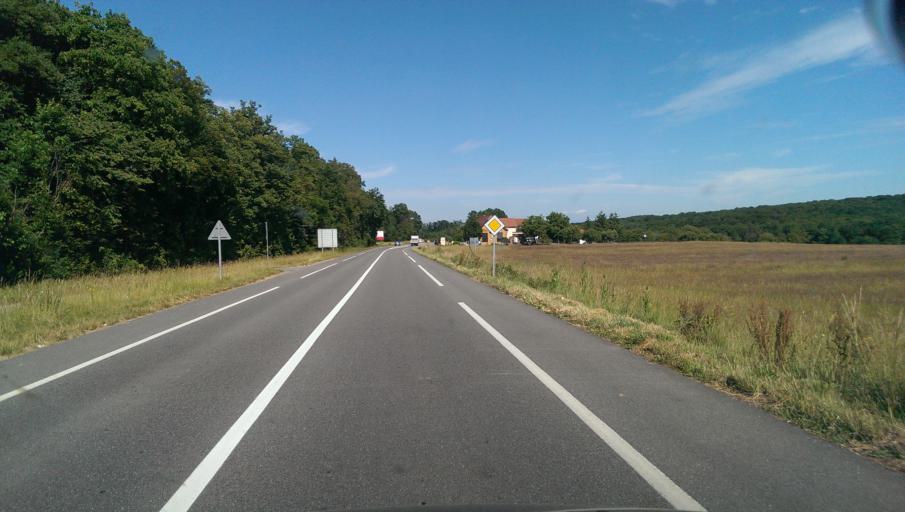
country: FR
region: Alsace
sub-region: Departement du Bas-Rhin
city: Monswiller
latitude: 48.7420
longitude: 7.3947
